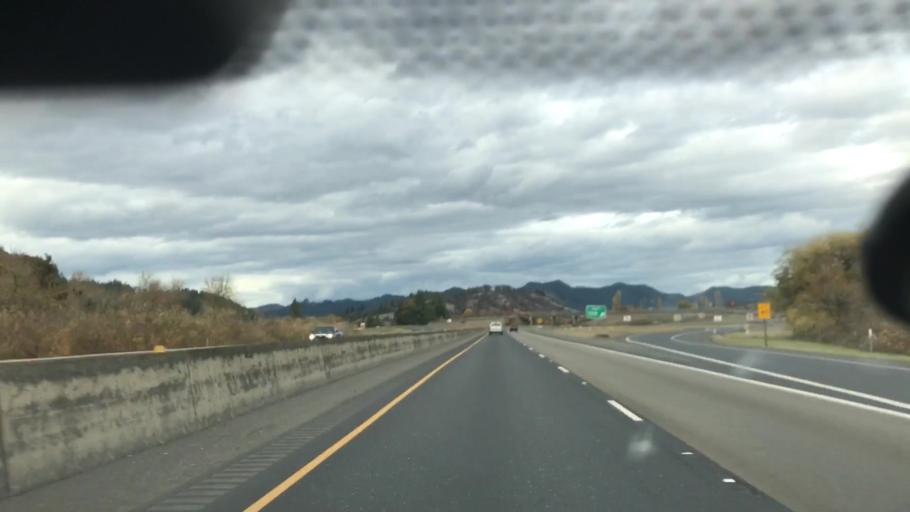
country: US
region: Oregon
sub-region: Douglas County
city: Yoncalla
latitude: 43.5592
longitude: -123.2823
